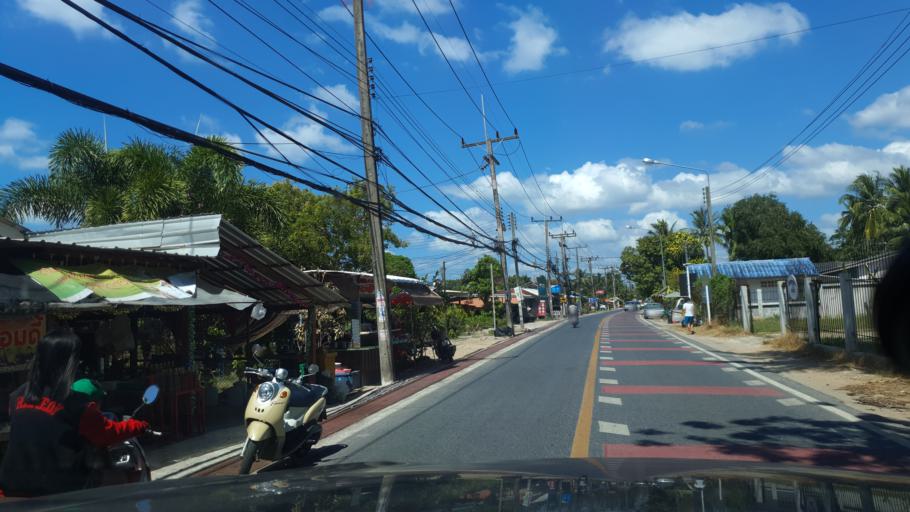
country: TH
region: Phuket
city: Thalang
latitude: 8.1243
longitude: 98.3082
